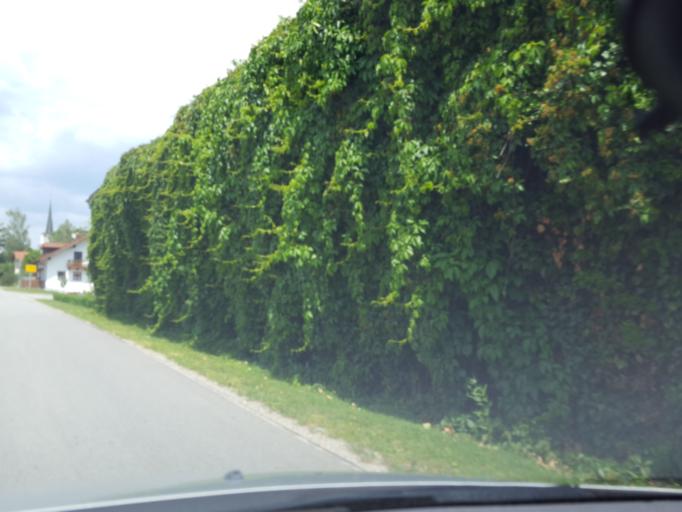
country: DE
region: Bavaria
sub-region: Upper Bavaria
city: Egglkofen
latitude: 48.4361
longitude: 12.4257
